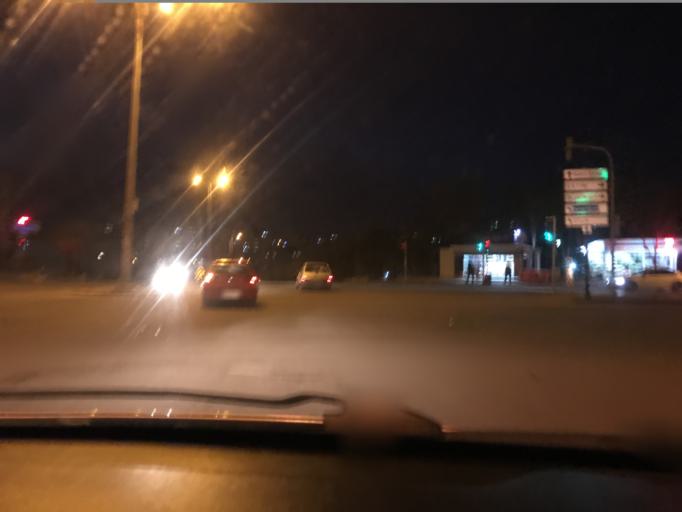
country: TR
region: Ankara
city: Batikent
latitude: 39.9616
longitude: 32.7325
